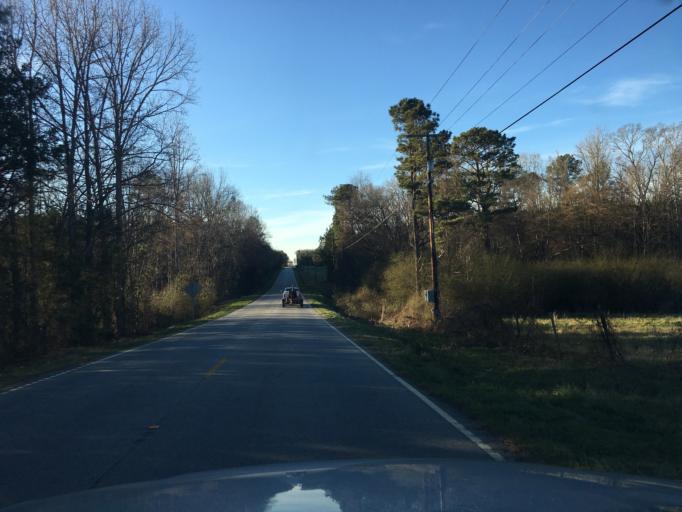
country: US
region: South Carolina
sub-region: Saluda County
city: Saluda
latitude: 34.0218
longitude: -81.7908
